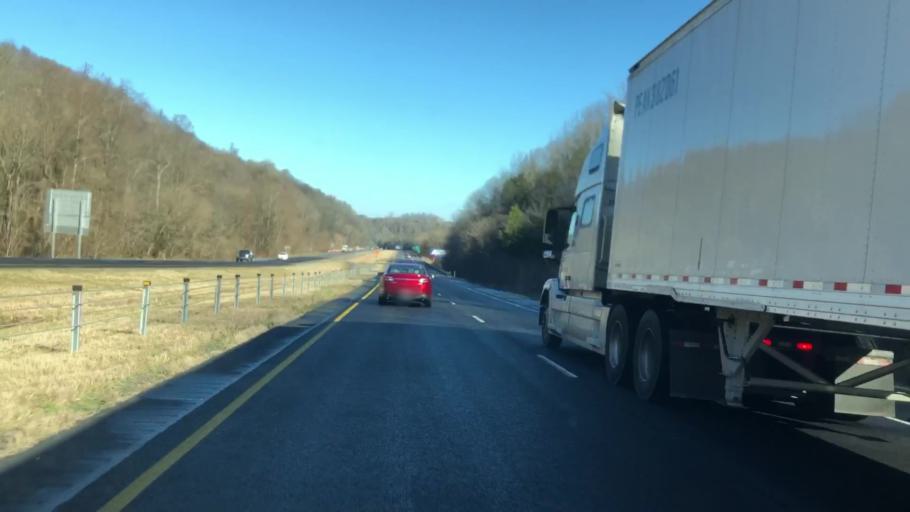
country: US
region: Alabama
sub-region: Limestone County
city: Ardmore
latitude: 34.9911
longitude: -86.8793
